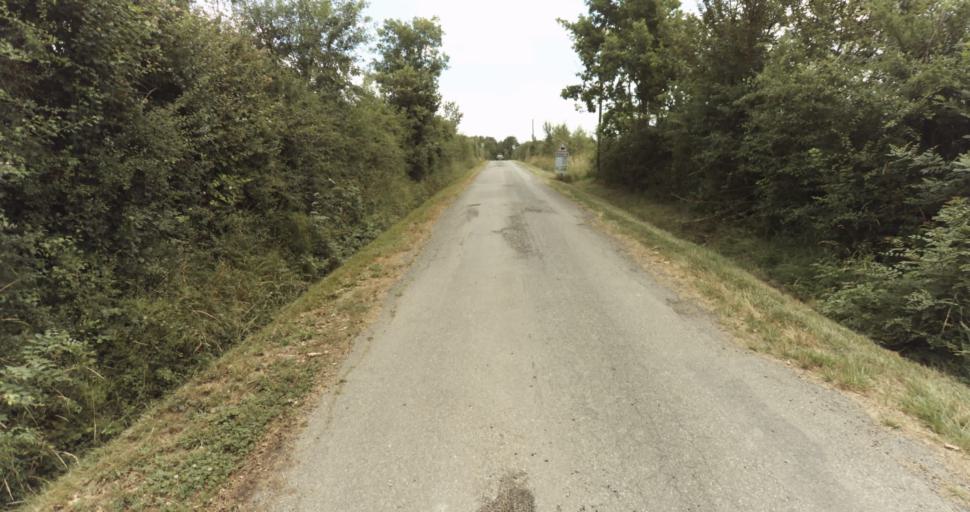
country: FR
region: Midi-Pyrenees
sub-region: Departement de la Haute-Garonne
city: Fontenilles
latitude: 43.5518
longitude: 1.1586
